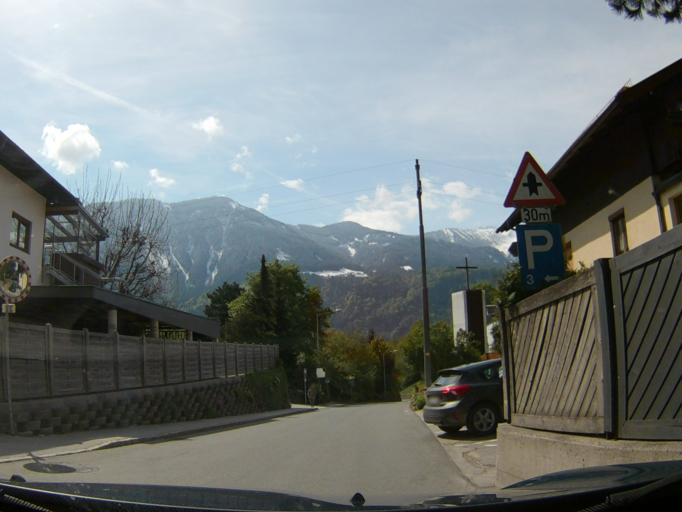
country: AT
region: Tyrol
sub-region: Politischer Bezirk Schwaz
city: Jenbach
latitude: 47.3943
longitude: 11.7713
